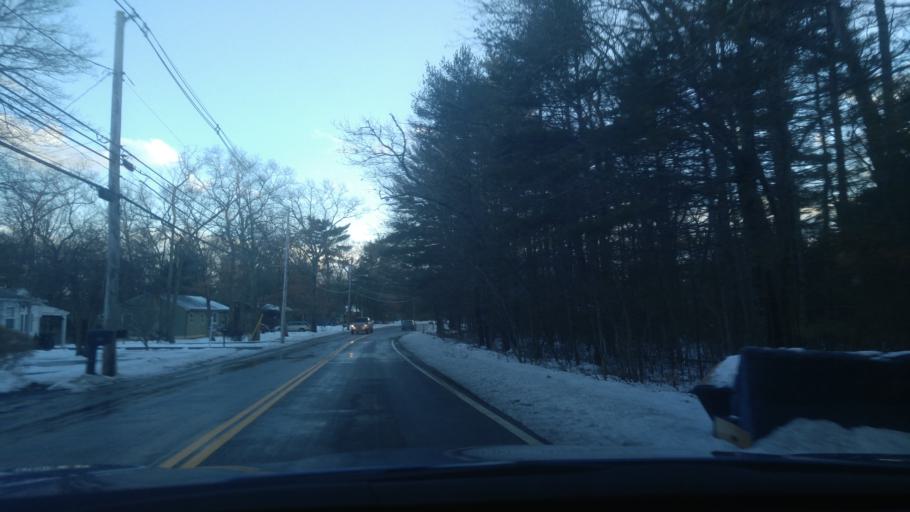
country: US
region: Rhode Island
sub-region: Kent County
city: West Greenwich
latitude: 41.6767
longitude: -71.6123
